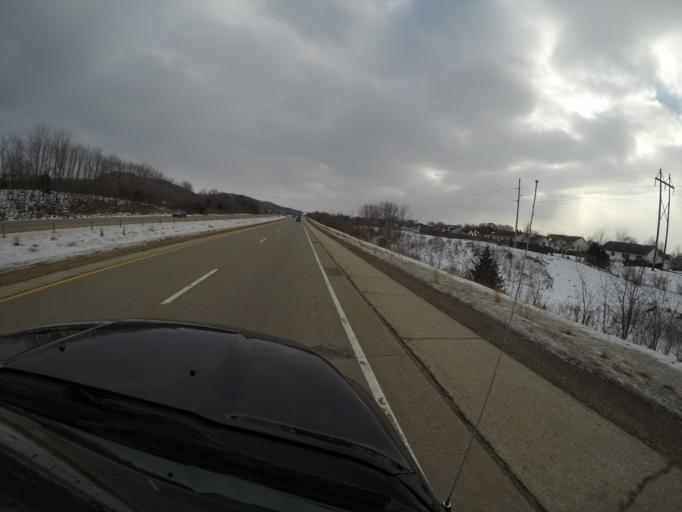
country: US
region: Wisconsin
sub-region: La Crosse County
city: Onalaska
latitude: 43.9092
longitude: -91.2321
